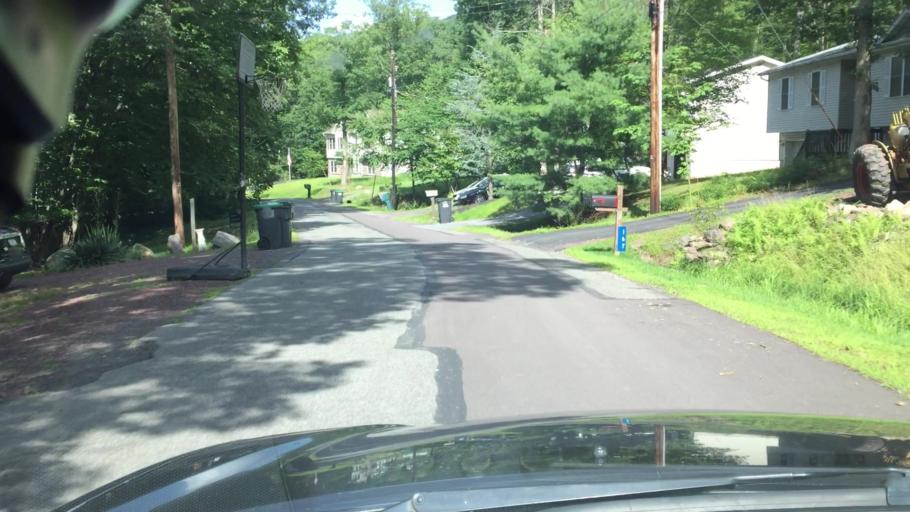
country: US
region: Pennsylvania
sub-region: Luzerne County
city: Freeland
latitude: 41.0360
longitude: -75.9340
